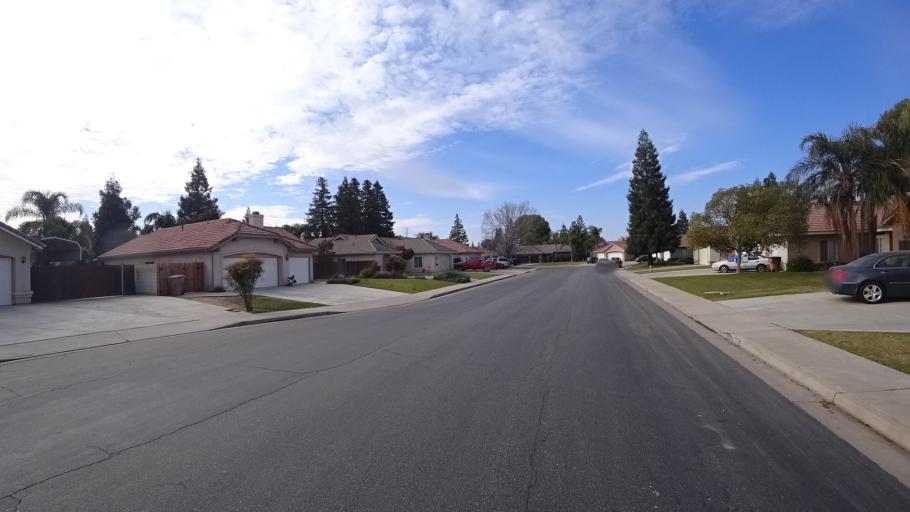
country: US
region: California
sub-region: Kern County
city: Greenacres
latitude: 35.3999
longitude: -119.0766
